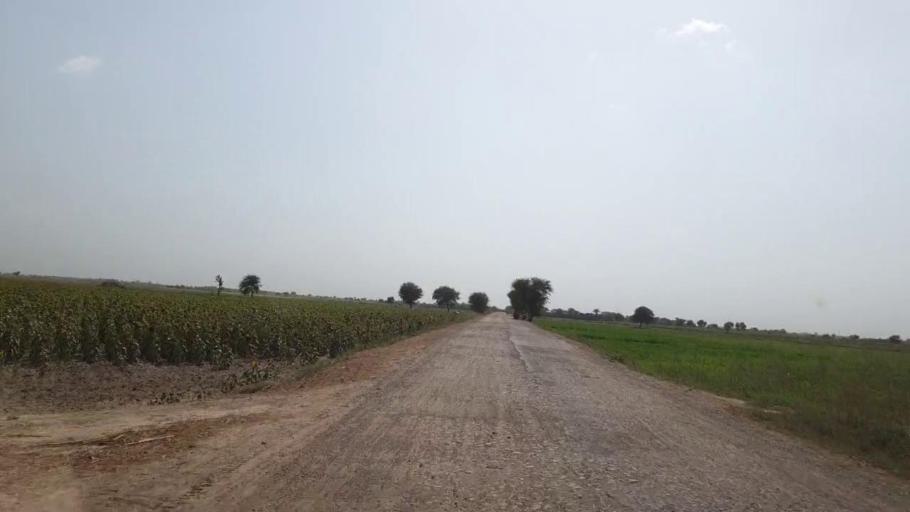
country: PK
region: Sindh
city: Rajo Khanani
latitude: 25.0458
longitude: 68.8763
